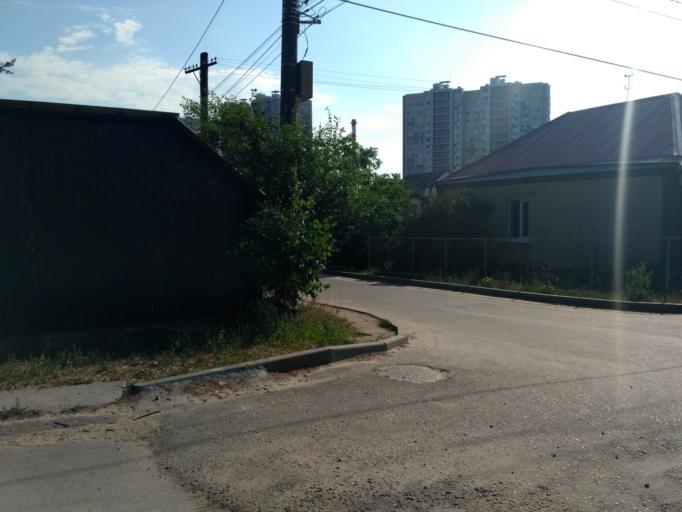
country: RU
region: Voronezj
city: Voronezh
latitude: 51.6759
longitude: 39.1357
